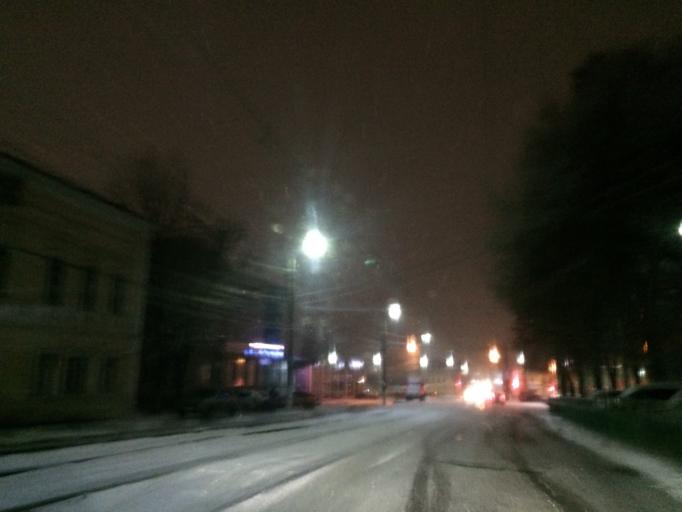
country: RU
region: Tula
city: Tula
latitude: 54.1985
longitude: 37.6379
